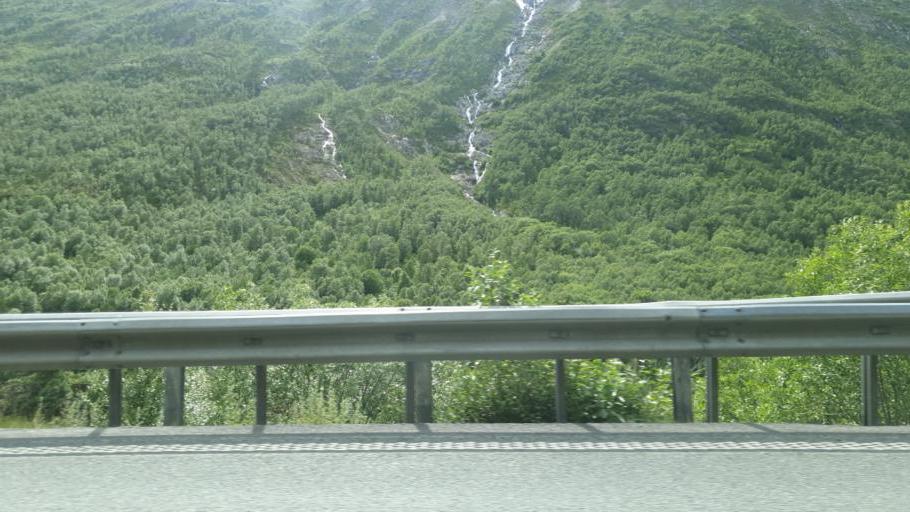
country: NO
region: Sor-Trondelag
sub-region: Oppdal
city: Oppdal
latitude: 62.4125
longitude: 9.6371
